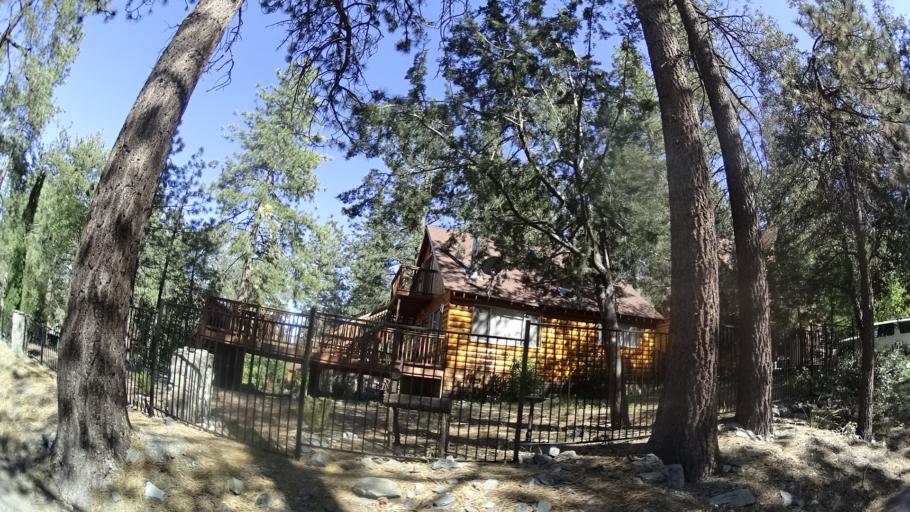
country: US
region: California
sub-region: San Bernardino County
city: Wrightwood
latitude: 34.3566
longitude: -117.6409
